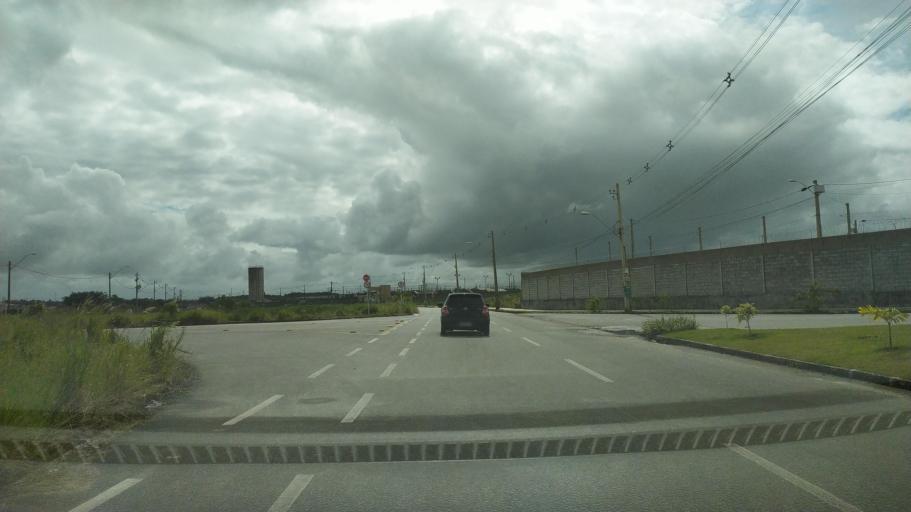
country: BR
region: Alagoas
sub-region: Satuba
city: Satuba
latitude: -9.5318
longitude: -35.7702
